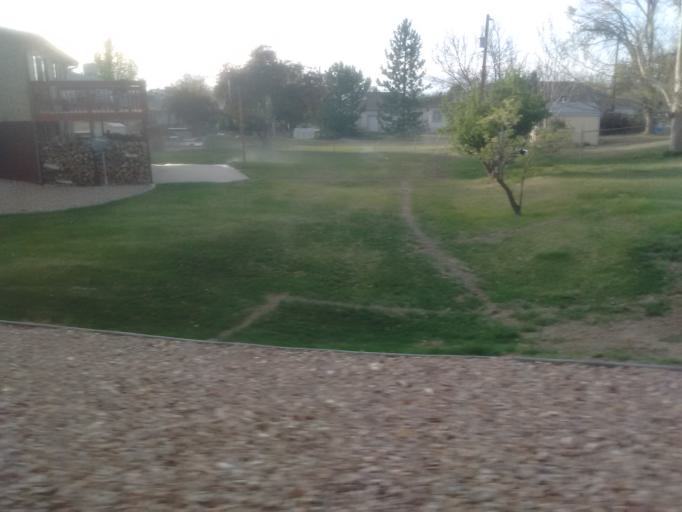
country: US
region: Colorado
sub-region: Mesa County
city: Grand Junction
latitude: 39.1084
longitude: -108.5630
